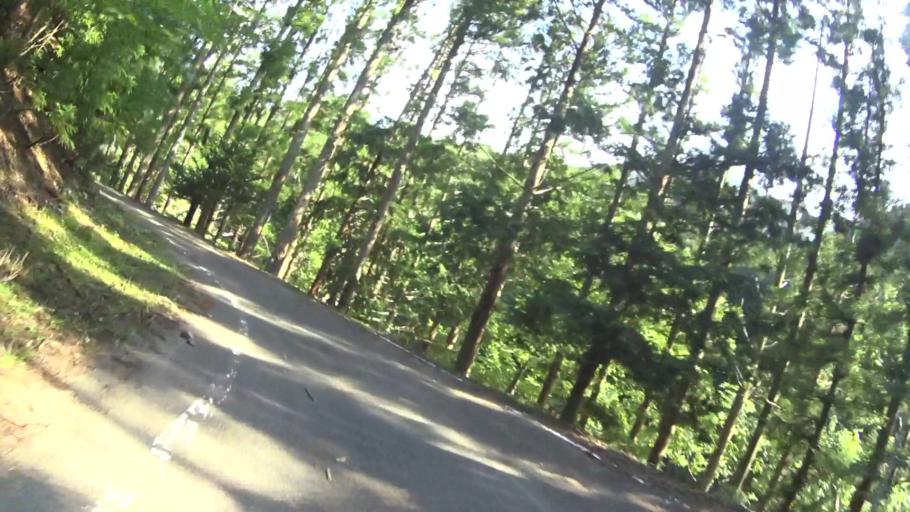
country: JP
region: Fukui
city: Obama
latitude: 35.2719
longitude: 135.6912
